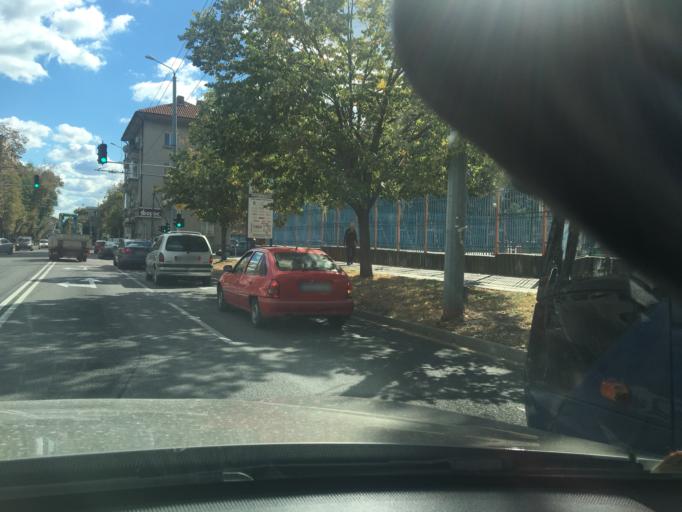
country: BG
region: Burgas
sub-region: Obshtina Burgas
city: Burgas
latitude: 42.4980
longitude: 27.4688
